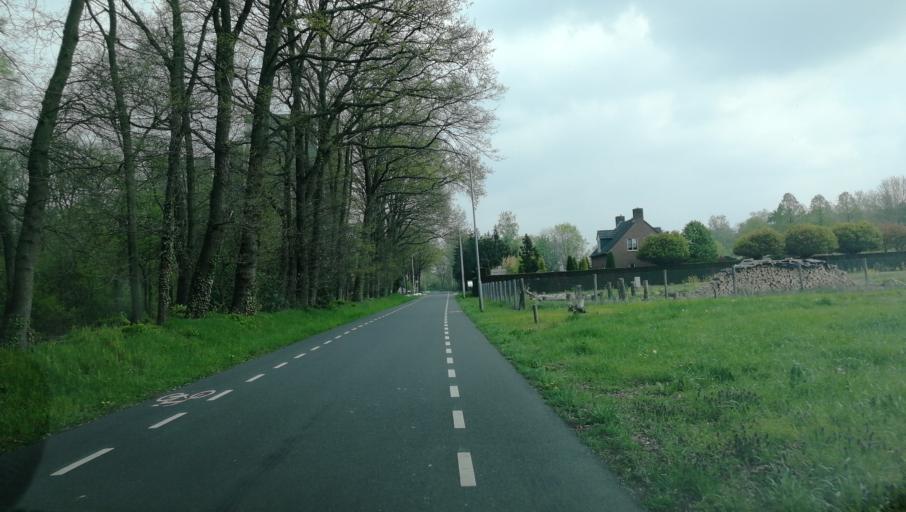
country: NL
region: Limburg
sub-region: Gemeente Venlo
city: Venlo
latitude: 51.3582
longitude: 6.1947
